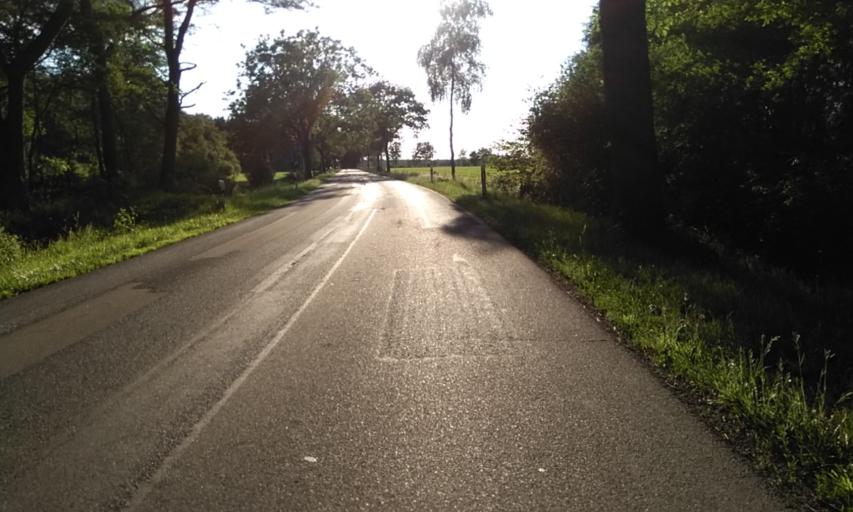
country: DE
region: Lower Saxony
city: Anderlingen
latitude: 53.3591
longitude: 9.3373
